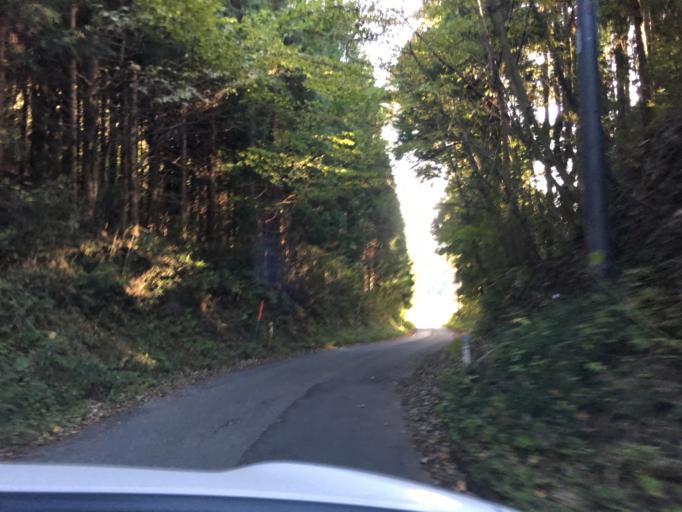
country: JP
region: Fukushima
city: Ishikawa
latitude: 37.2419
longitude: 140.6086
